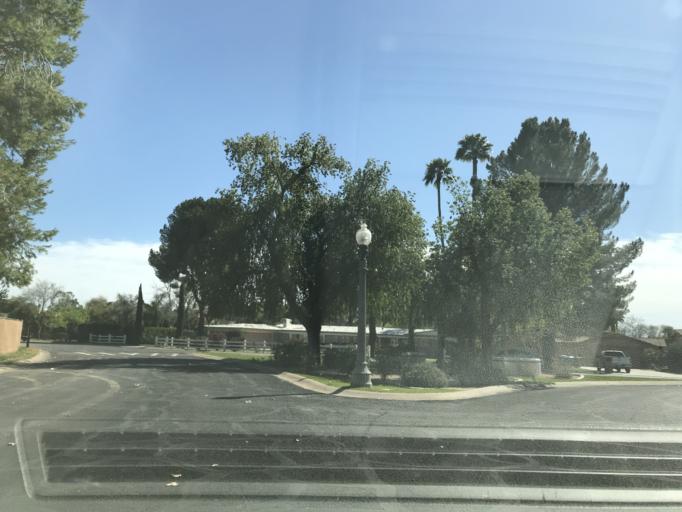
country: US
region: Arizona
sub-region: Maricopa County
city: Phoenix
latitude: 33.5206
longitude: -112.0761
